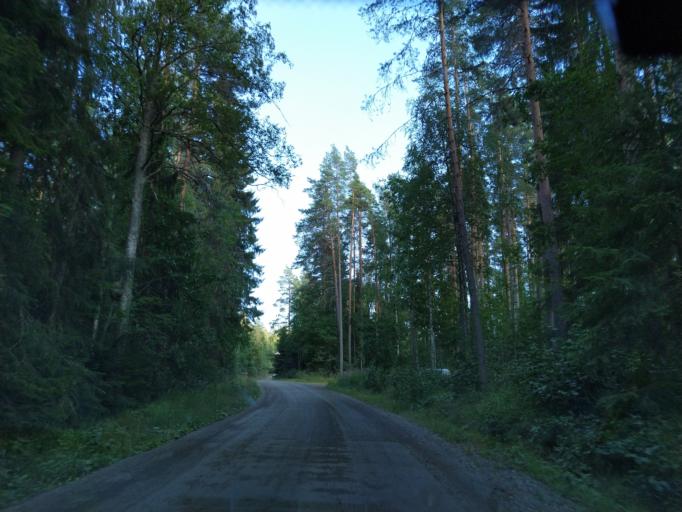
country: FI
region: Central Finland
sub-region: Jaemsae
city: Kuhmoinen
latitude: 61.6877
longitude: 24.9643
